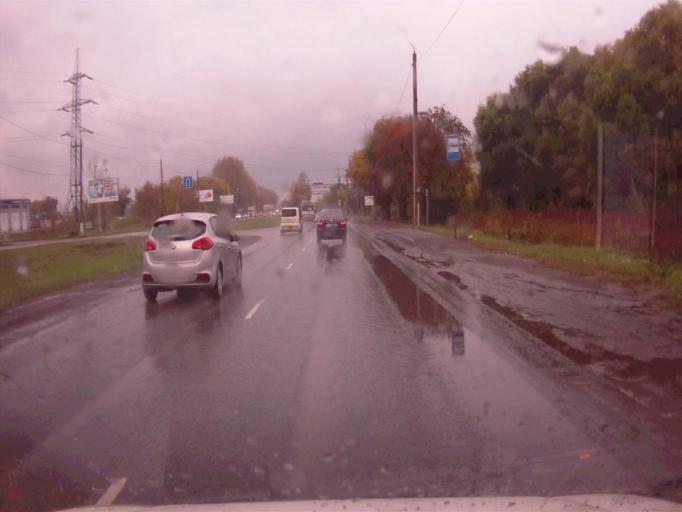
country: RU
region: Chelyabinsk
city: Dolgoderevenskoye
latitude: 55.2471
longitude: 61.3583
